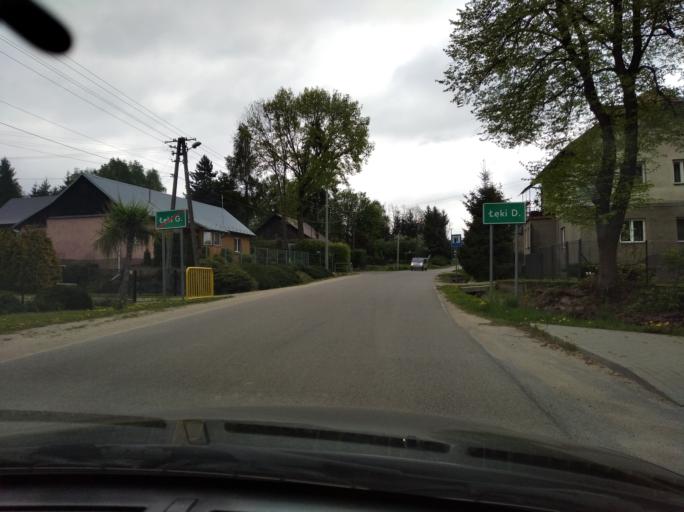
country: PL
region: Subcarpathian Voivodeship
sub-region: Powiat debicki
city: Leki Dolne
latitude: 49.9753
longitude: 21.2154
